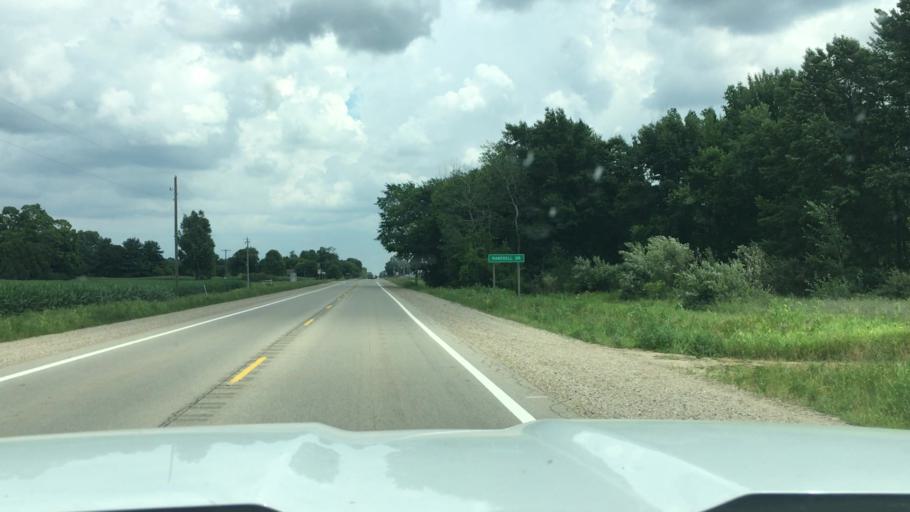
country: US
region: Michigan
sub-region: Kent County
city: Cedar Springs
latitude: 43.1763
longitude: -85.4344
